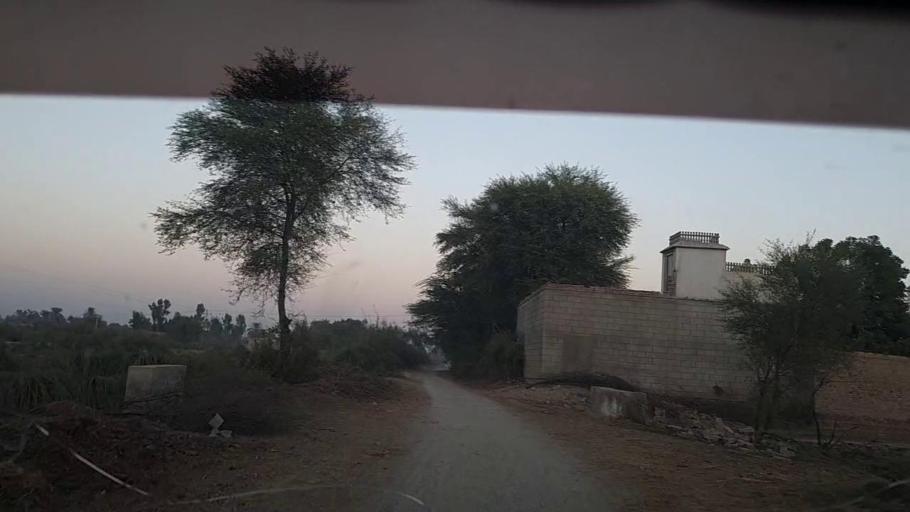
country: PK
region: Sindh
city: Ratodero
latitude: 27.8634
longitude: 68.2616
